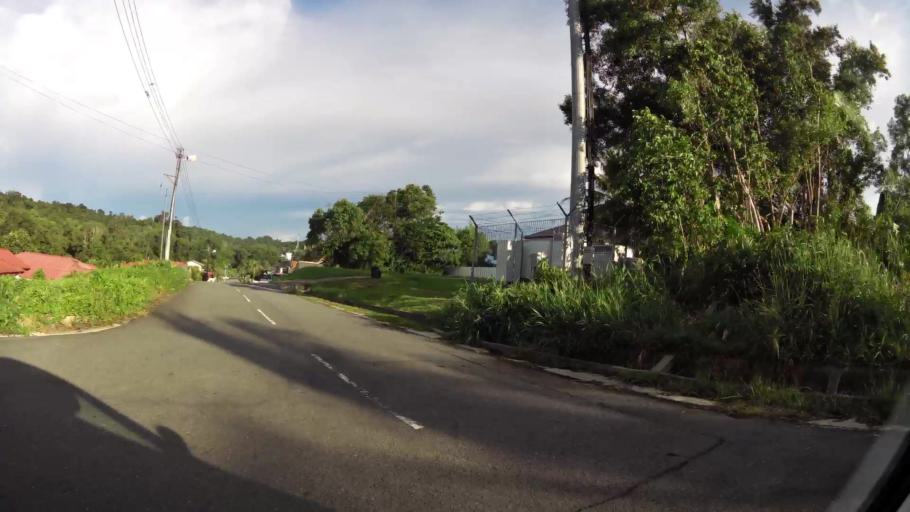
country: BN
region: Brunei and Muara
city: Bandar Seri Begawan
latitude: 4.9687
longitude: 114.9854
